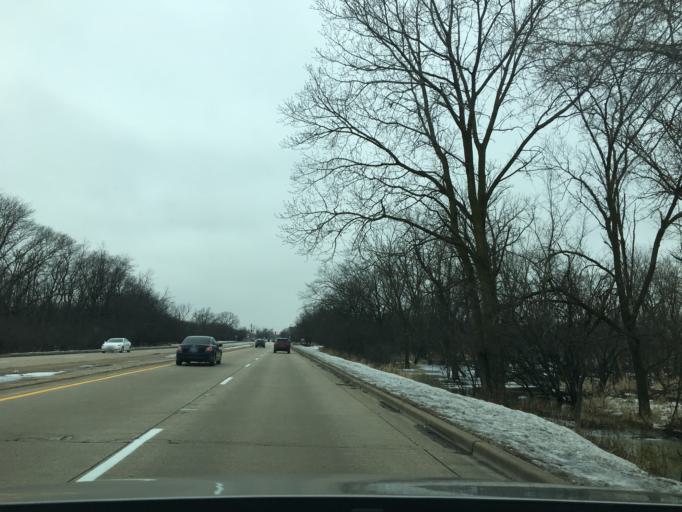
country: US
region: Illinois
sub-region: Cook County
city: Schiller Park
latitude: 41.9662
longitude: -87.8569
